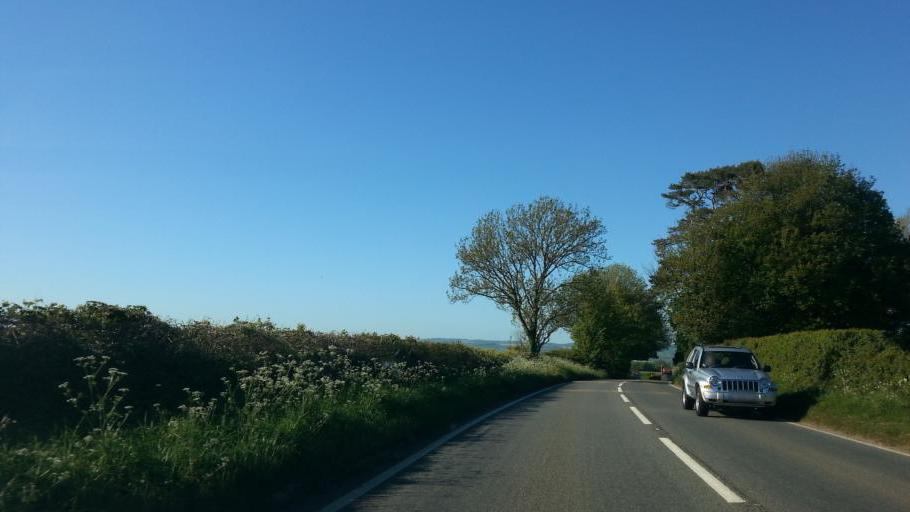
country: GB
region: England
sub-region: Somerset
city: Castle Cary
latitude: 51.0858
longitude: -2.5055
